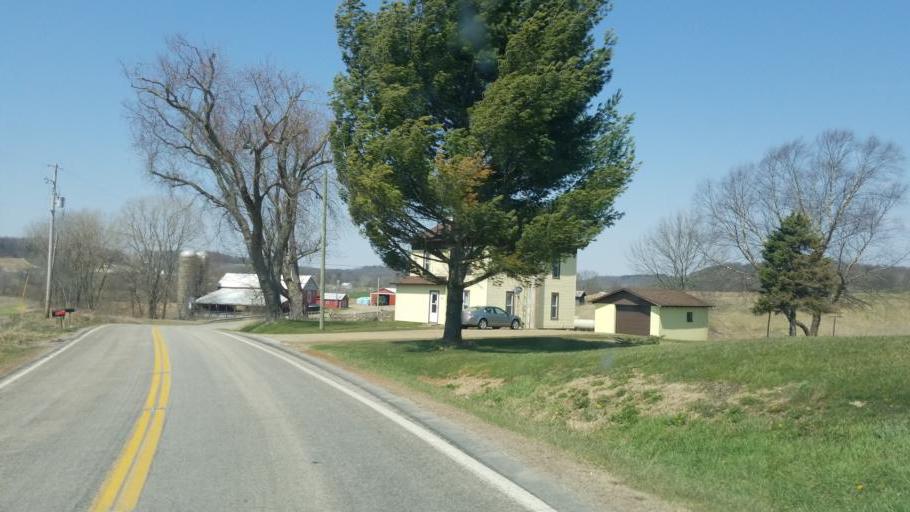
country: US
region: Ohio
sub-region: Ashland County
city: Loudonville
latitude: 40.6919
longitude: -82.1464
